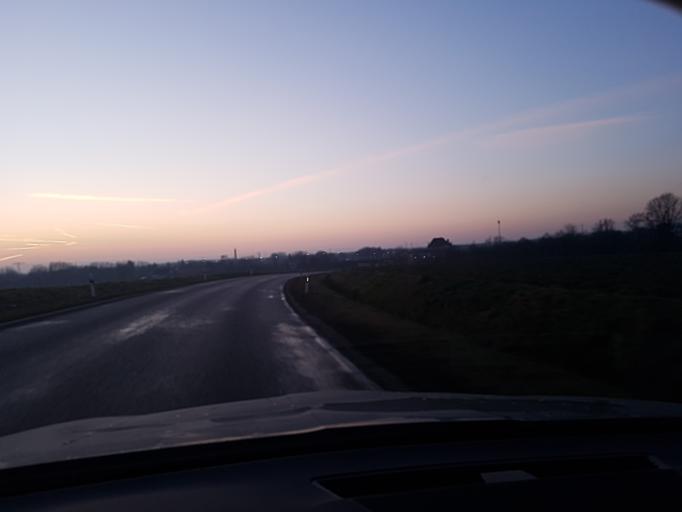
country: DE
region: Brandenburg
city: Doberlug-Kirchhain
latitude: 51.6205
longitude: 13.5709
